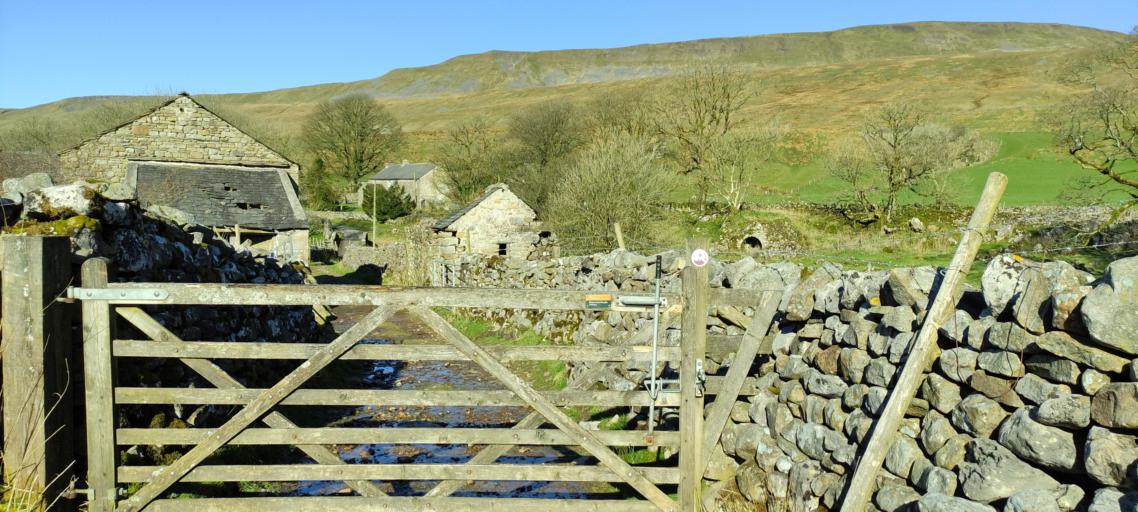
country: GB
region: England
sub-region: North Yorkshire
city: Ingleton
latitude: 54.2165
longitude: -2.3783
